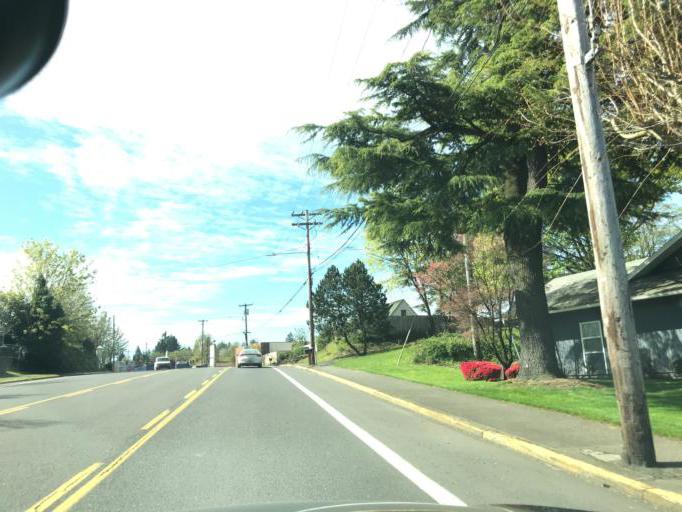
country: US
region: Oregon
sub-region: Multnomah County
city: Lents
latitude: 45.4989
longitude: -122.5683
